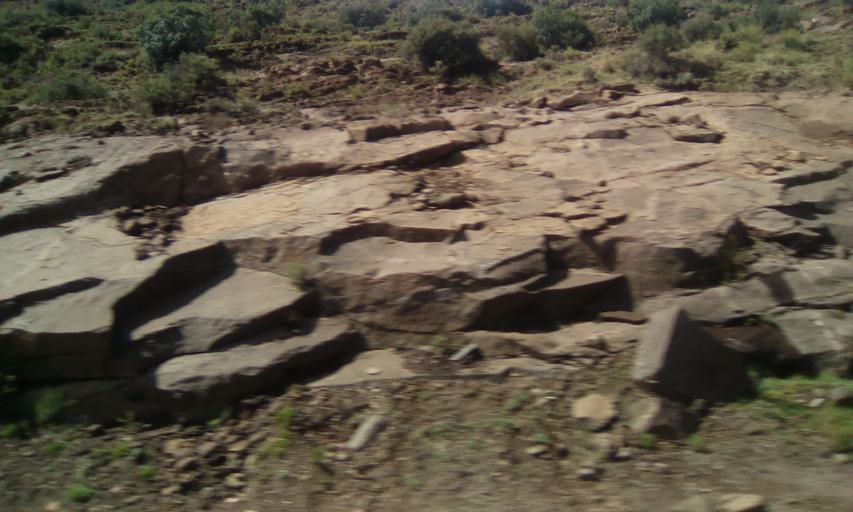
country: LS
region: Maseru
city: Nako
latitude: -29.6562
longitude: 27.8349
